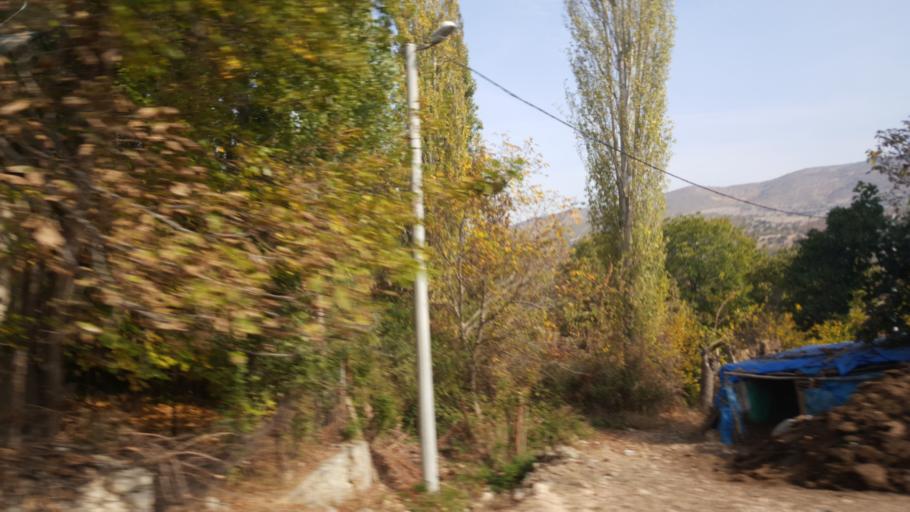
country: TR
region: Eskisehir
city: Mihaliccik
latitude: 39.9831
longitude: 31.3580
